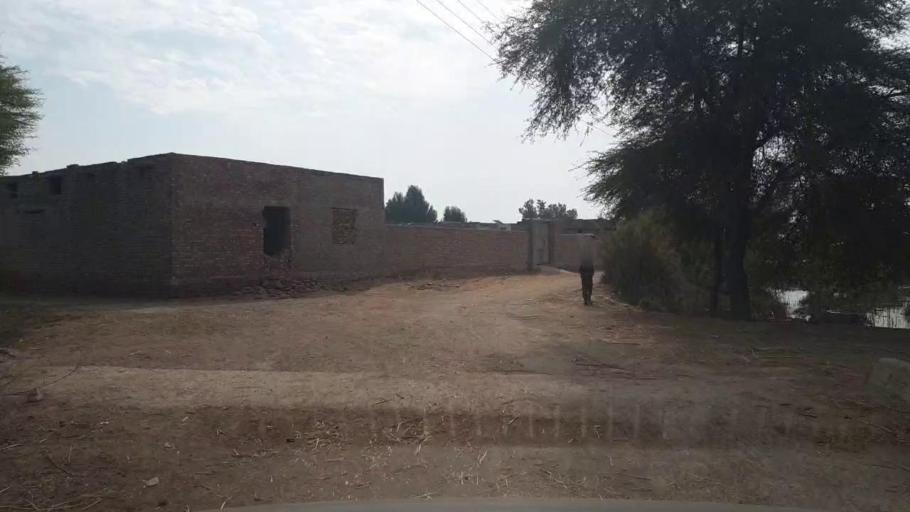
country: PK
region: Sindh
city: Hala
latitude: 26.0006
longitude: 68.4039
